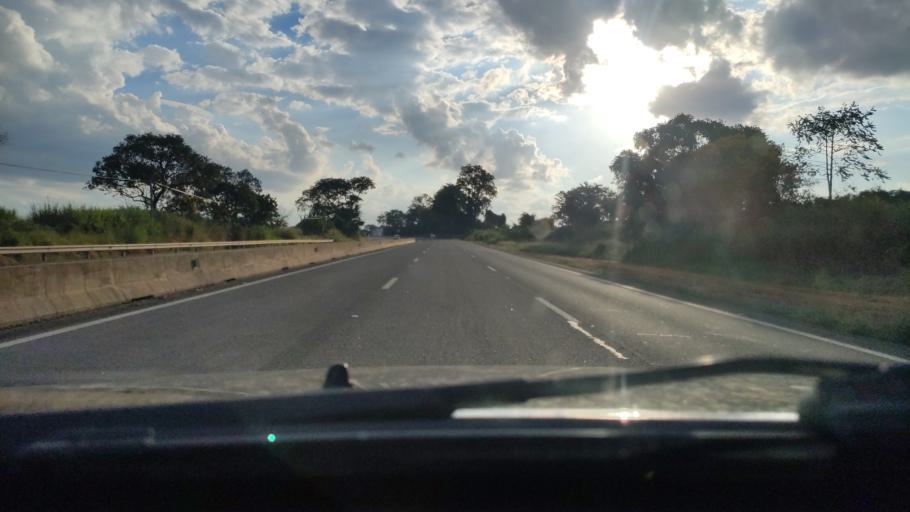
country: BR
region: Sao Paulo
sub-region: Mogi-Mirim
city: Mogi Mirim
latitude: -22.4506
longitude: -47.0803
